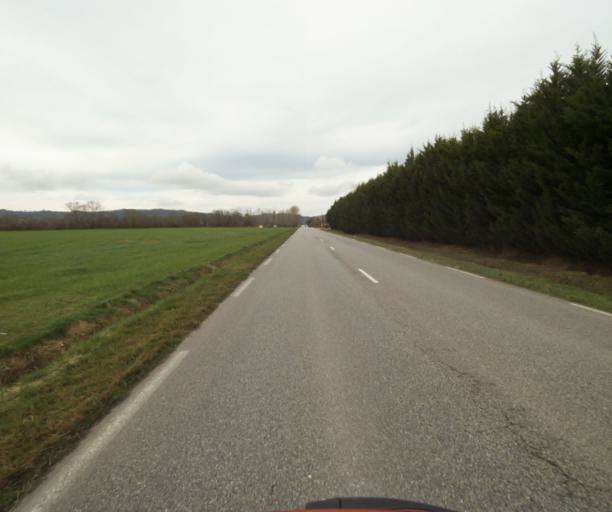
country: FR
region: Midi-Pyrenees
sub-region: Departement de l'Ariege
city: La Tour-du-Crieu
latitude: 43.0991
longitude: 1.6476
